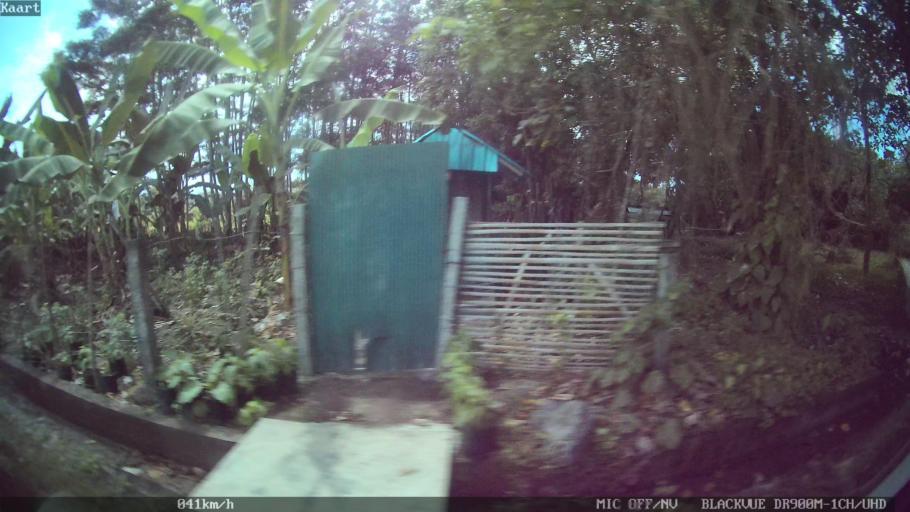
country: ID
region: Bali
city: Banjar Desa
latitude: -8.5841
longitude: 115.2873
